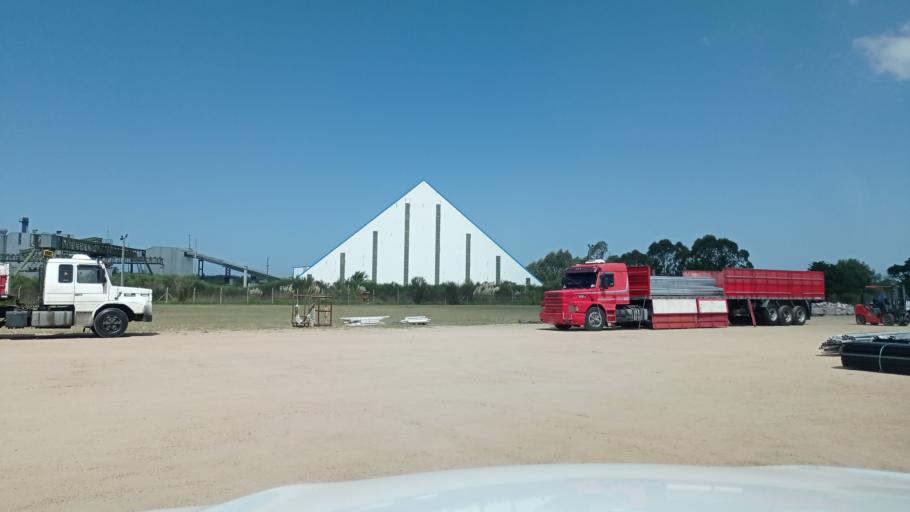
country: UY
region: Canelones
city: La Paz
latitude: -34.8195
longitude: -56.1934
